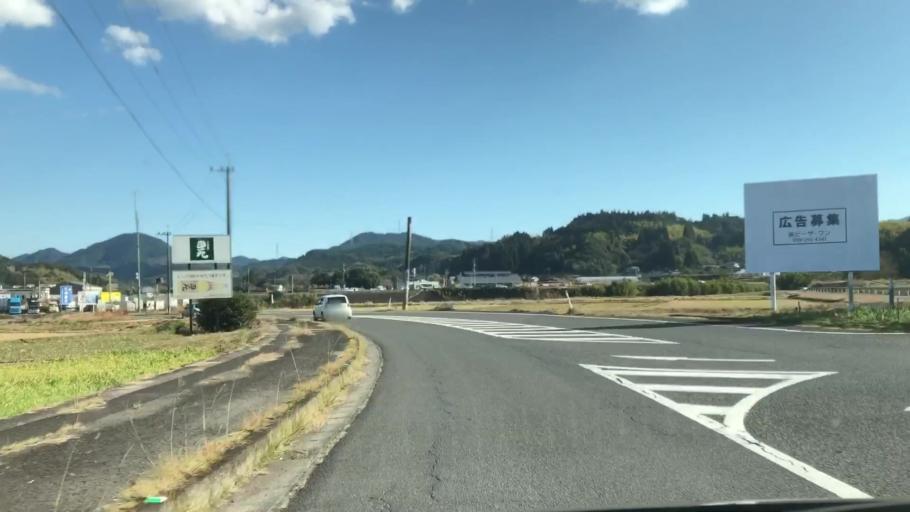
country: JP
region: Kagoshima
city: Satsumasendai
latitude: 31.7949
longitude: 130.4395
